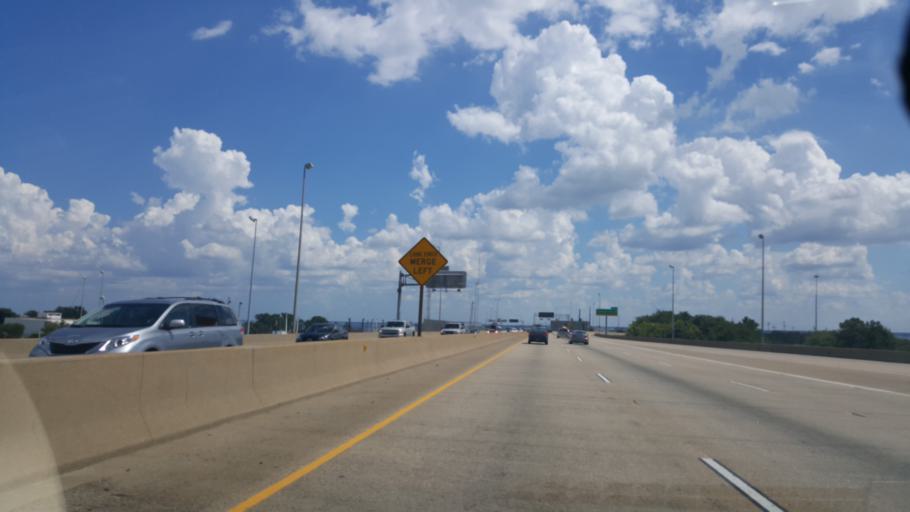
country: US
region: Virginia
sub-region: City of Newport News
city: Newport News
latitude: 36.9713
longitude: -76.4181
